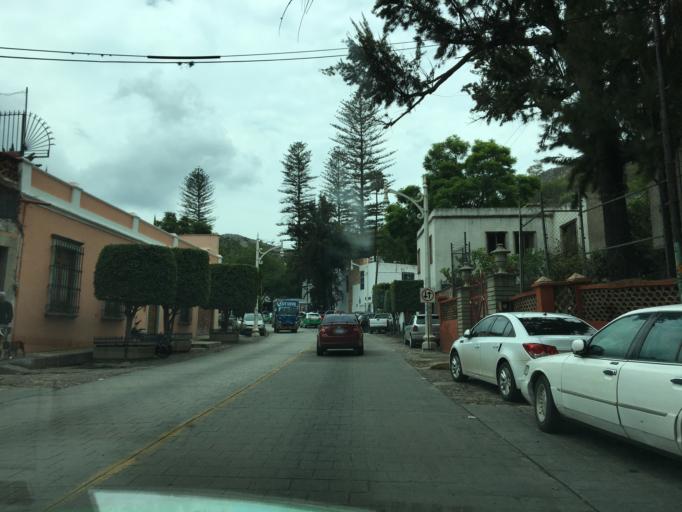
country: MX
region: Guanajuato
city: Guanajuato
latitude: 21.0046
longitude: -101.2478
